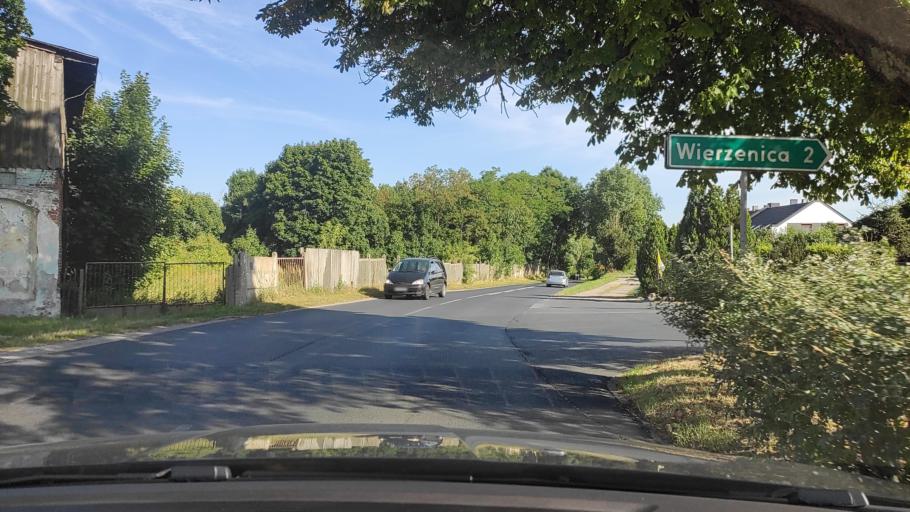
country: PL
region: Greater Poland Voivodeship
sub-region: Powiat poznanski
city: Kobylnica
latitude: 52.4783
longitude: 17.0952
